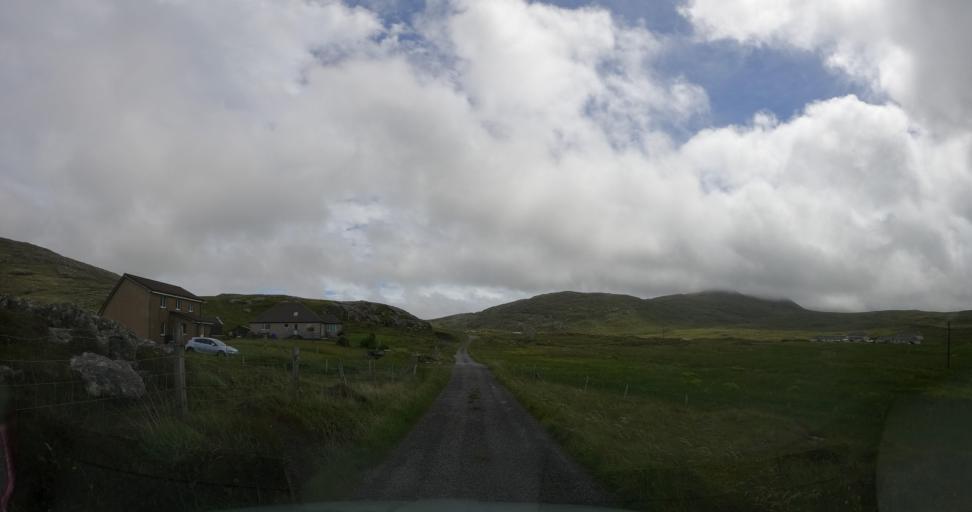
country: GB
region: Scotland
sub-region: Eilean Siar
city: Barra
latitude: 57.0037
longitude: -7.4848
